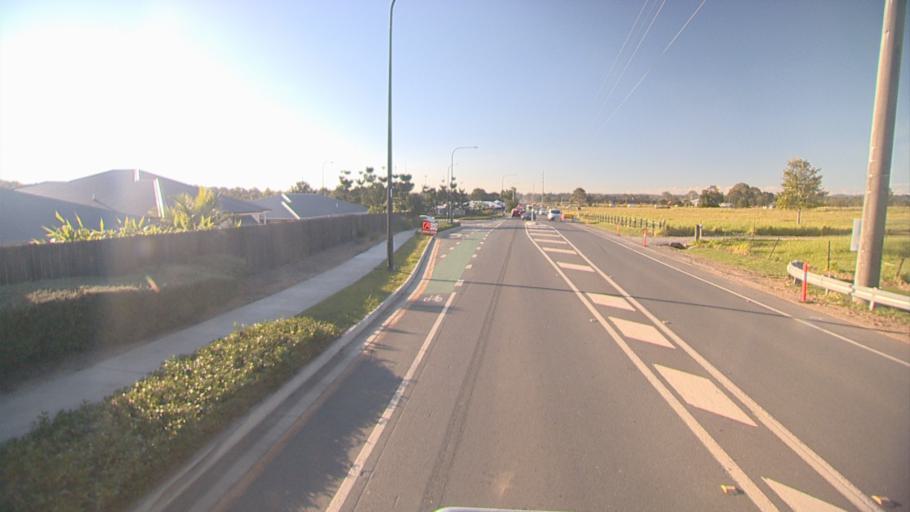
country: AU
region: Queensland
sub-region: Logan
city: Waterford West
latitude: -27.7119
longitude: 153.1161
